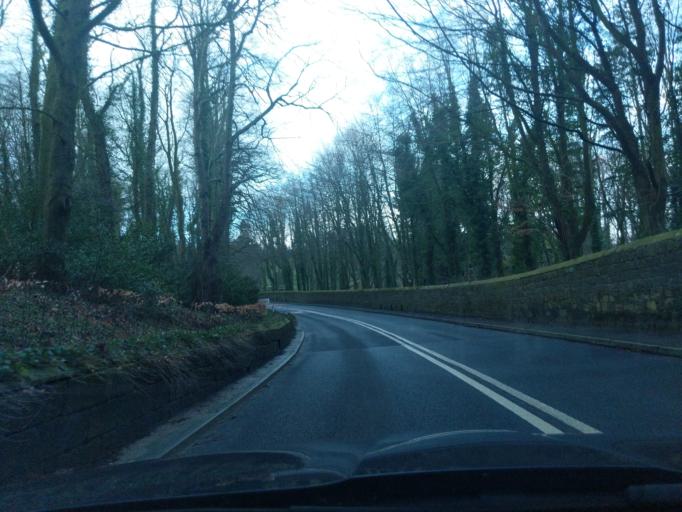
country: GB
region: England
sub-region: Northumberland
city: Alnwick
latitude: 55.4148
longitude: -1.6960
